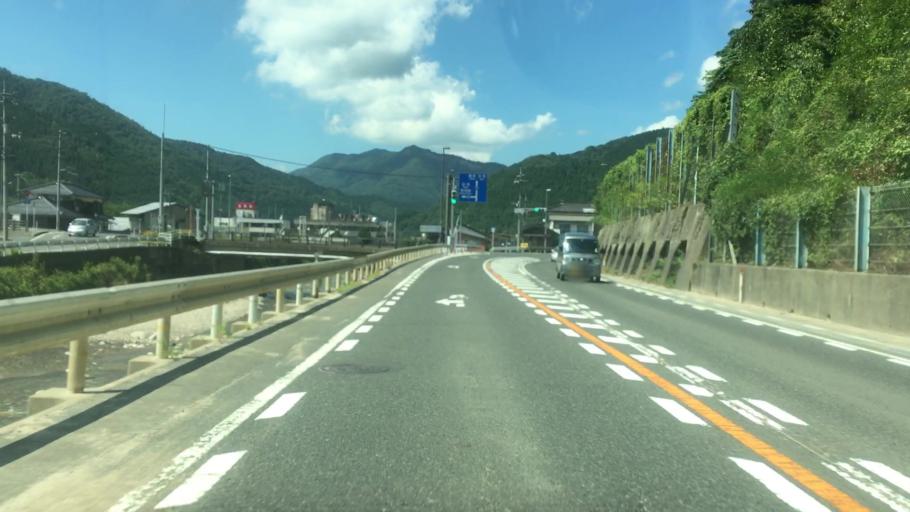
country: JP
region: Tottori
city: Tottori
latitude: 35.2617
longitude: 134.2275
